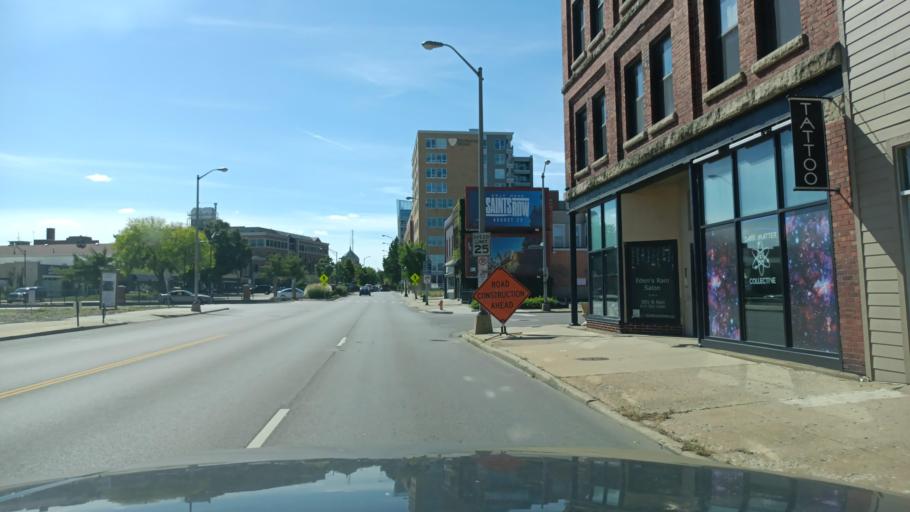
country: US
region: Illinois
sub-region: Champaign County
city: Champaign
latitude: 40.1206
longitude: -88.2436
